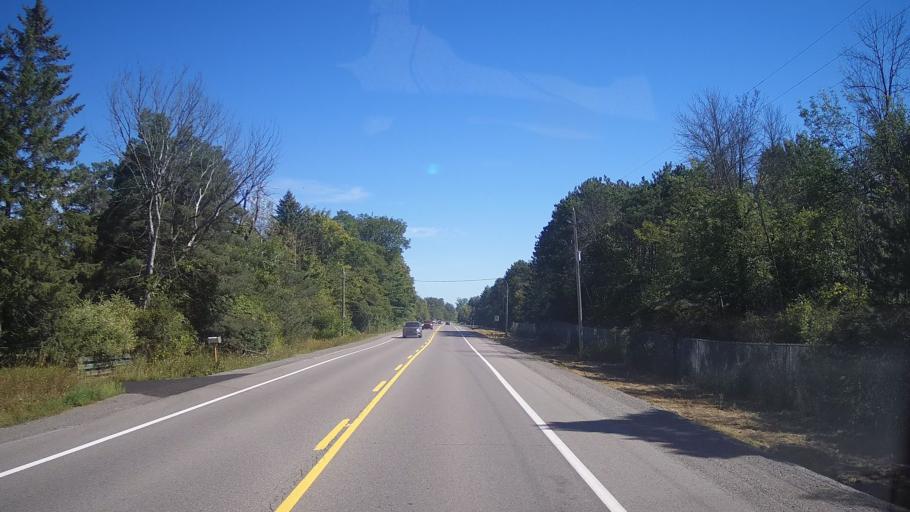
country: CA
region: Ontario
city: Bells Corners
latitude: 45.0581
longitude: -75.6761
